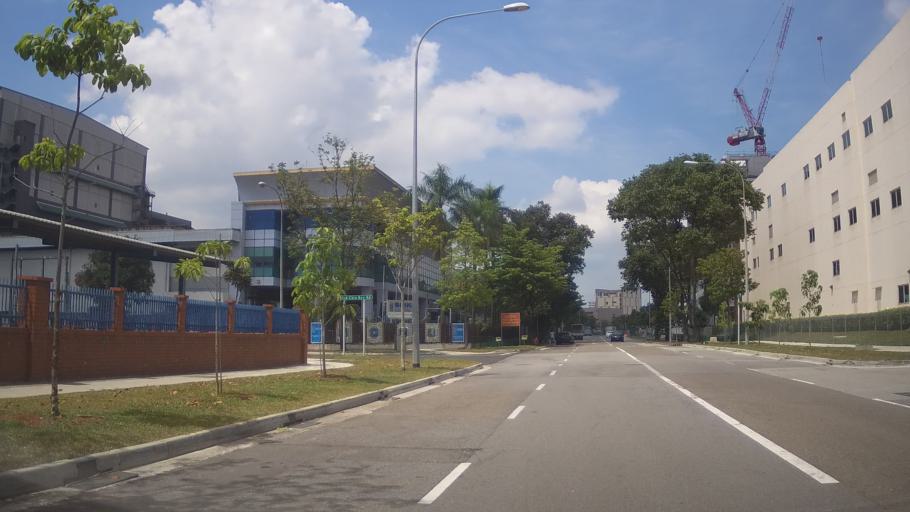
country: MY
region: Johor
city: Johor Bahru
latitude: 1.3365
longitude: 103.7155
